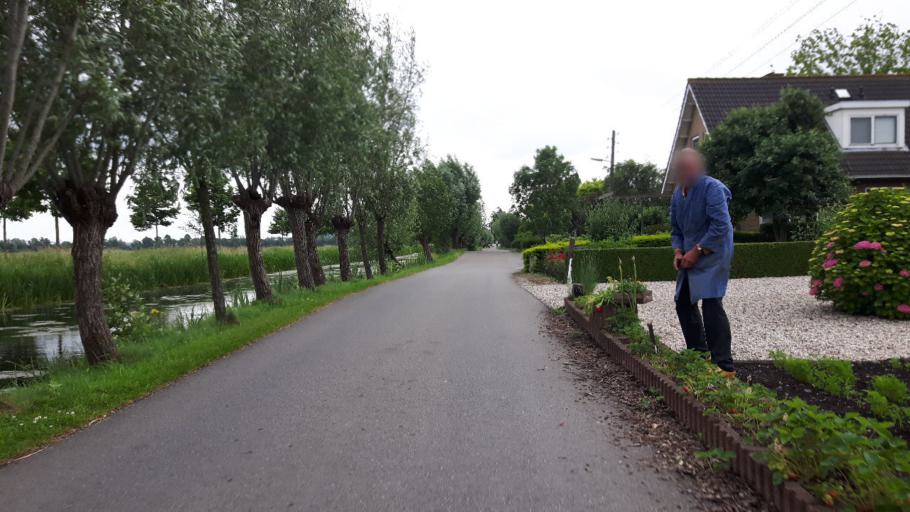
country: NL
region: Utrecht
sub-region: Gemeente Oudewater
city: Oudewater
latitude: 52.0424
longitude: 4.8550
